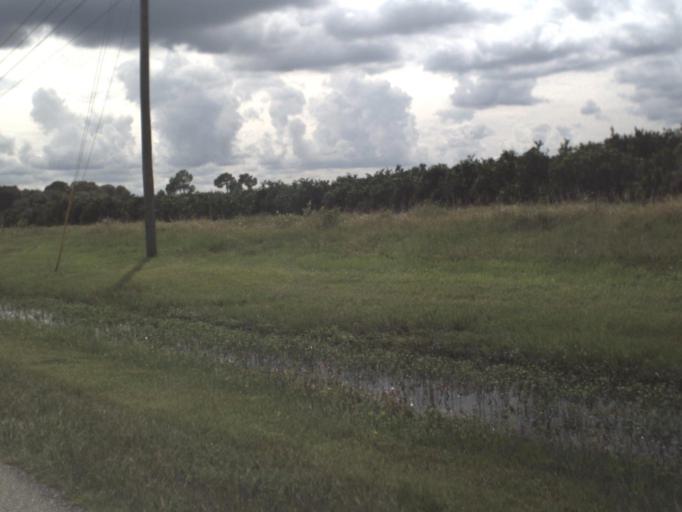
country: US
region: Florida
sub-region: DeSoto County
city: Nocatee
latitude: 27.0174
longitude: -81.7605
